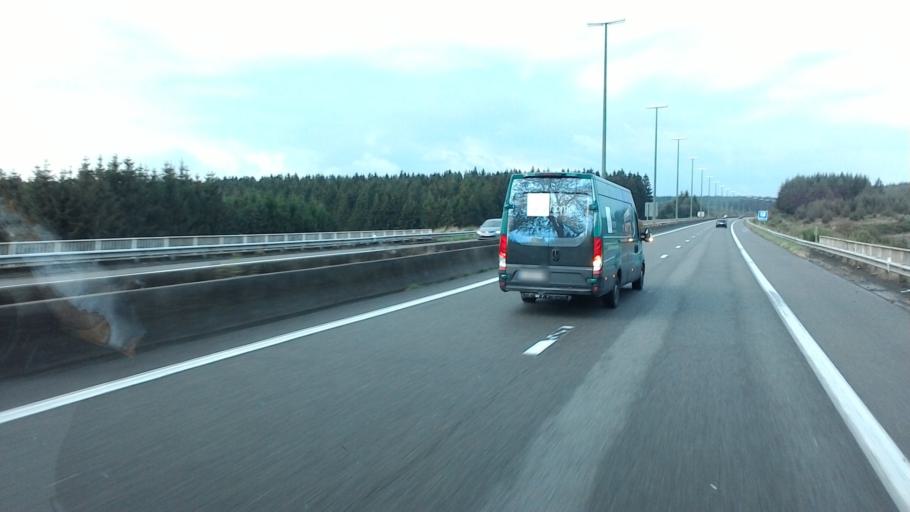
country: BE
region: Wallonia
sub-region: Province du Luxembourg
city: Bastogne
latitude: 50.0290
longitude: 5.7003
